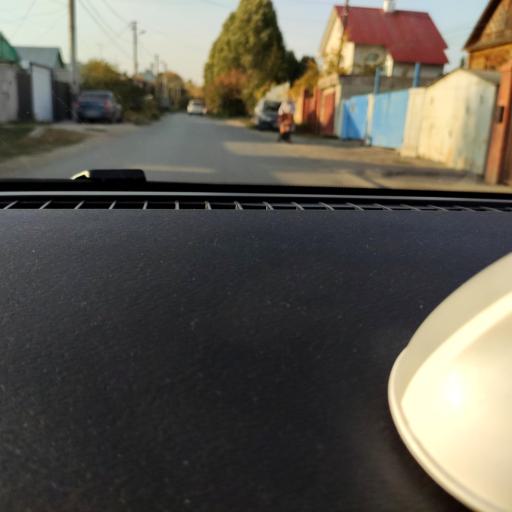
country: RU
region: Samara
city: Samara
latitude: 53.2320
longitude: 50.2360
